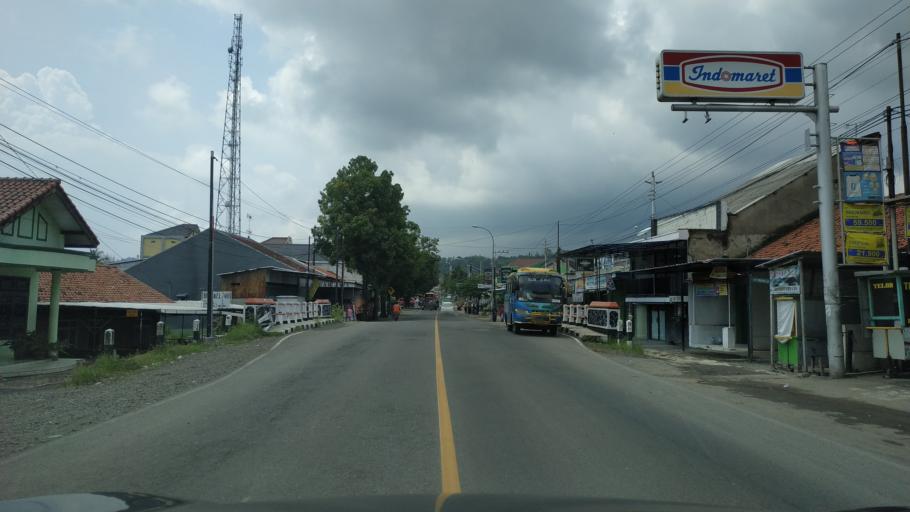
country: ID
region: Central Java
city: Lebaksiu
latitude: -7.0467
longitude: 109.1438
